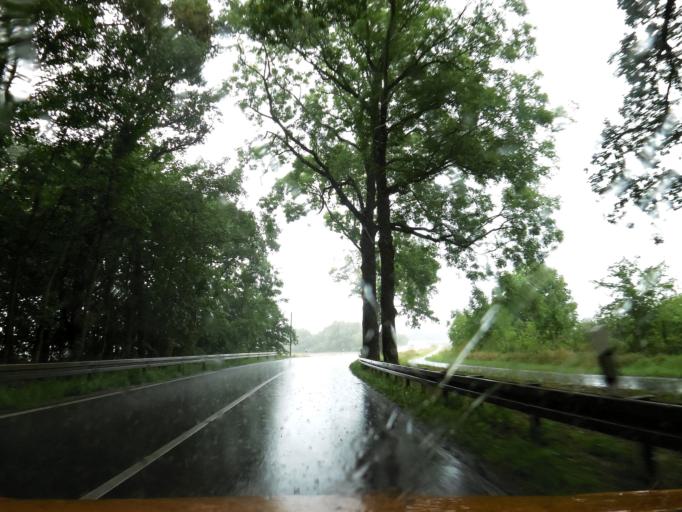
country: DE
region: Brandenburg
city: Werder
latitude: 52.4369
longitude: 12.9894
